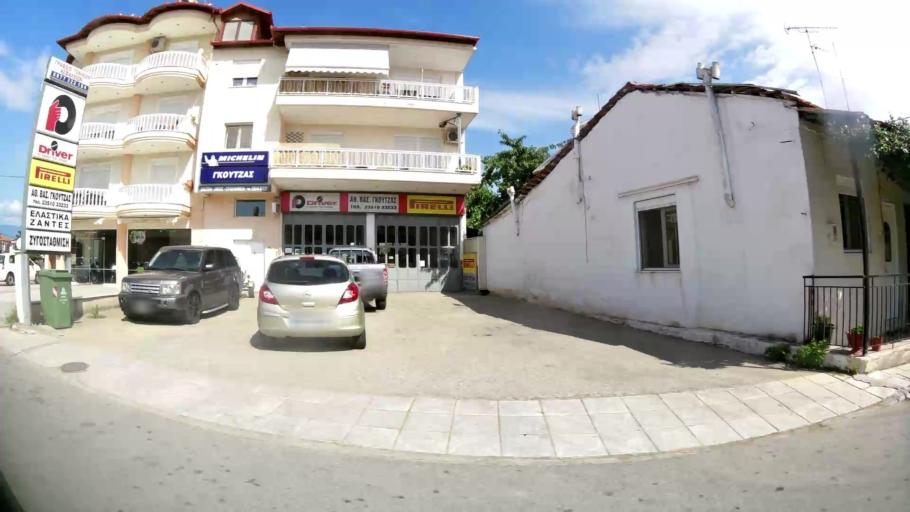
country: GR
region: Central Macedonia
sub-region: Nomos Pierias
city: Katerini
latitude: 40.2811
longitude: 22.4995
